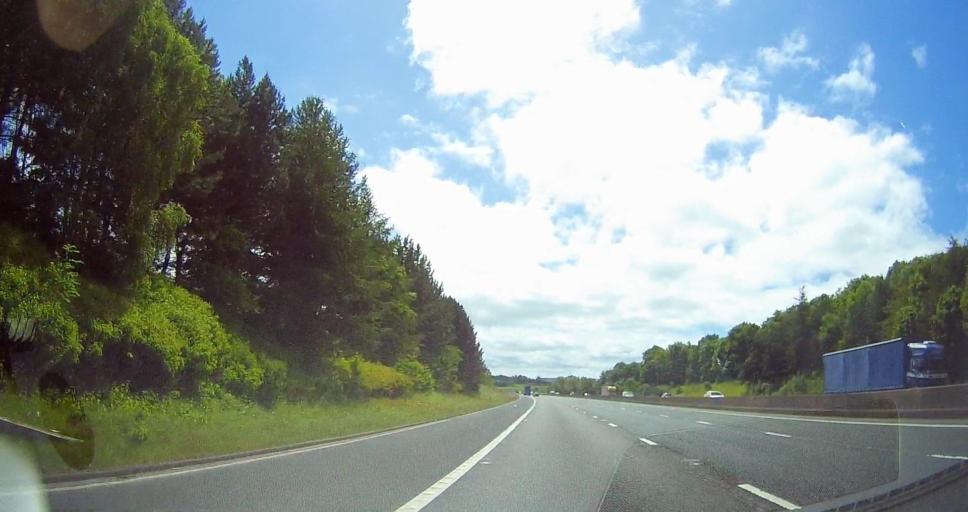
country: GB
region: England
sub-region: Cumbria
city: Penrith
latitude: 54.6929
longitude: -2.7868
